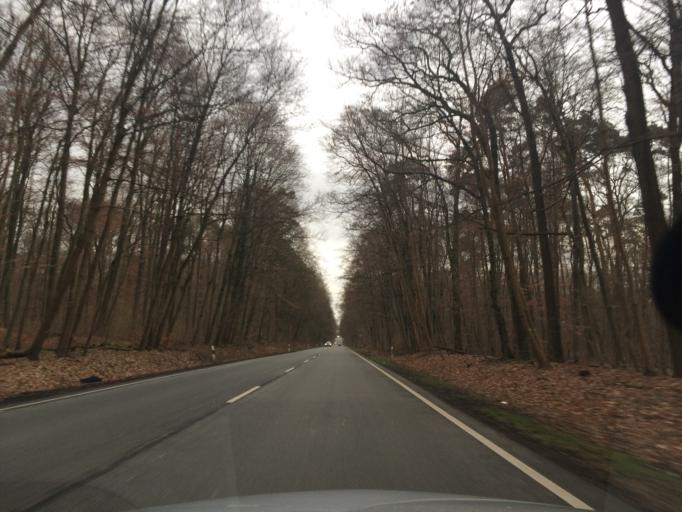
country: DE
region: Hesse
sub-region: Regierungsbezirk Darmstadt
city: Neu Isenburg
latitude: 50.0703
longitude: 8.6937
